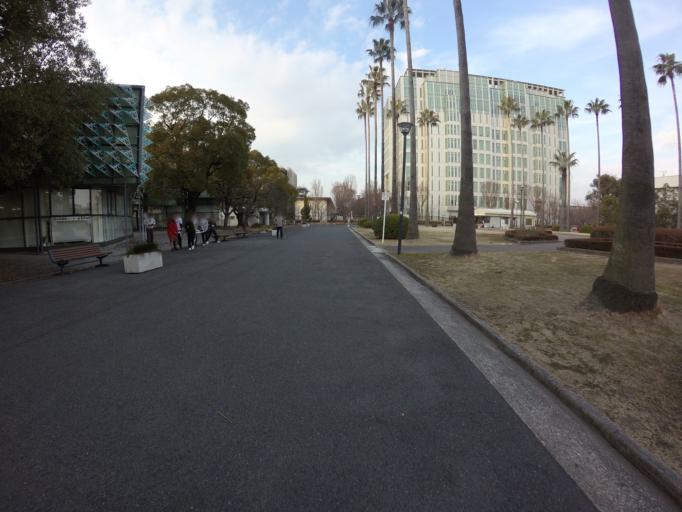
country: JP
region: Osaka
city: Sakai
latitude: 34.5915
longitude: 135.5047
